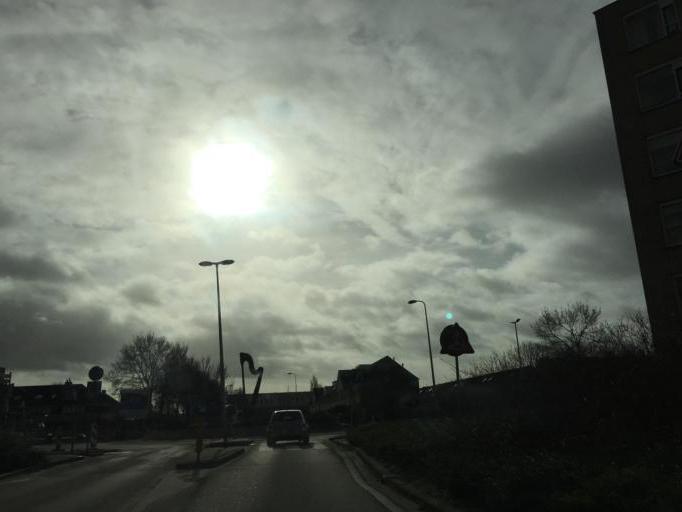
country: NL
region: South Holland
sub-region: Gemeente Capelle aan den IJssel
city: Capelle-West
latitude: 51.9177
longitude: 4.5599
